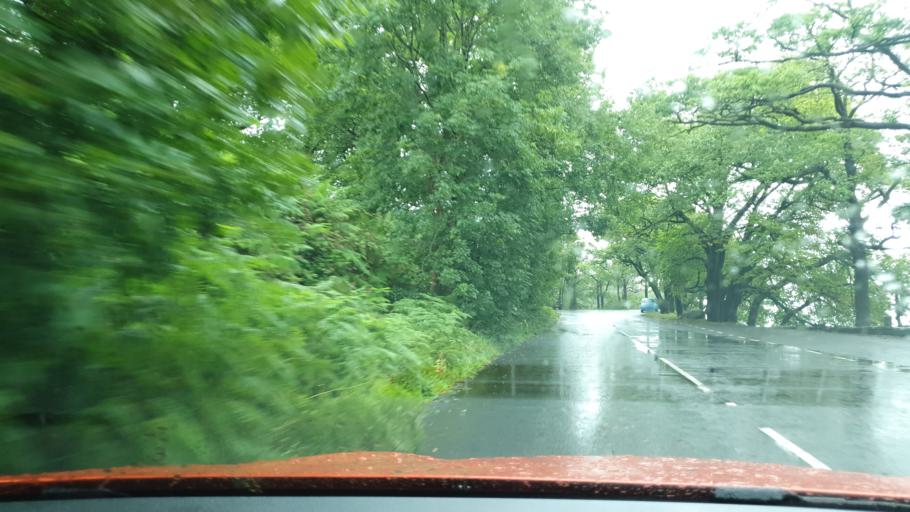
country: GB
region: England
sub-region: Cumbria
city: Ulverston
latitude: 54.3175
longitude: -3.0920
